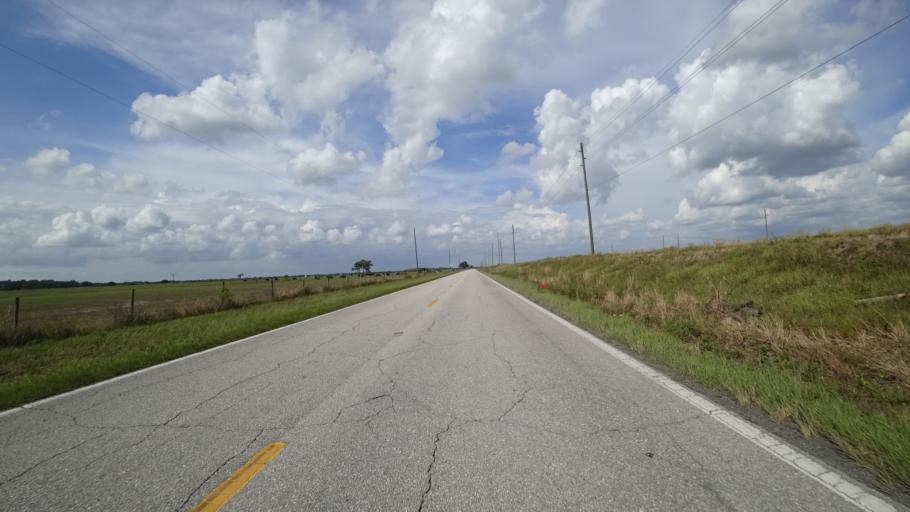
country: US
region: Florida
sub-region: Hardee County
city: Wauchula
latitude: 27.5198
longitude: -82.0731
